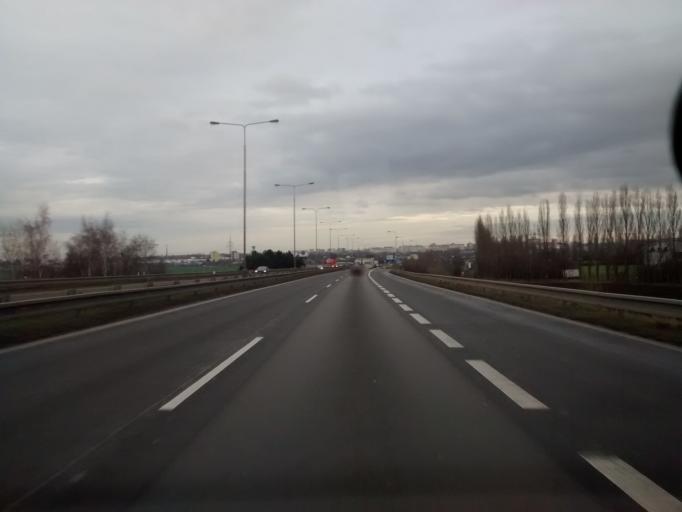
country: CZ
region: Central Bohemia
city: Zdiby
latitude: 50.1590
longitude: 14.4820
